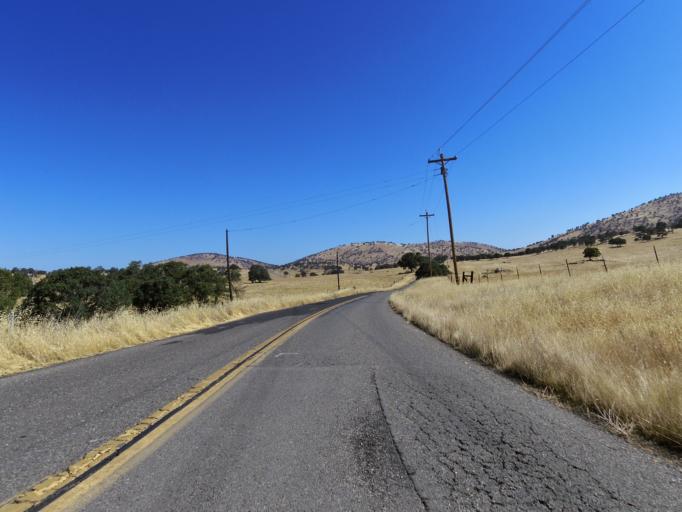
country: US
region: California
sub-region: Merced County
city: Planada
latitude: 37.5980
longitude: -120.3083
